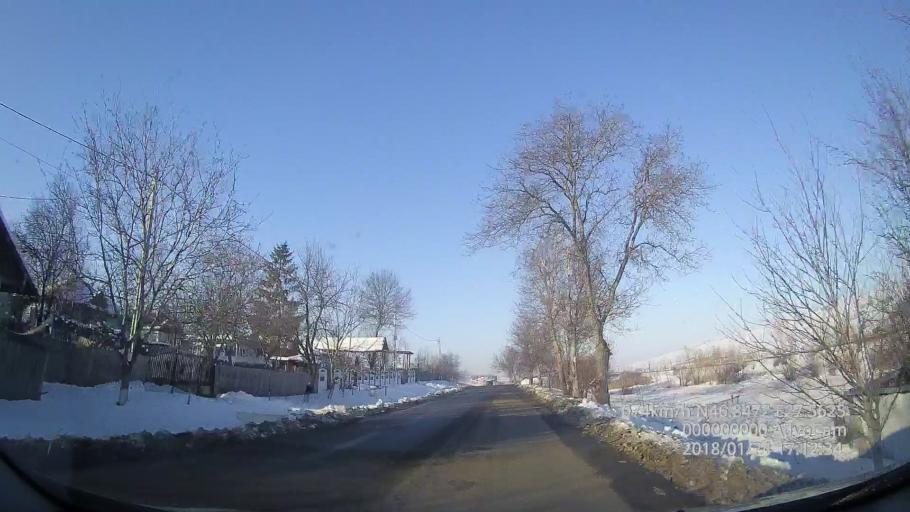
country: RO
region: Vaslui
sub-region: Comuna Rebricea
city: Rebricea
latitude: 46.8478
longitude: 27.5625
